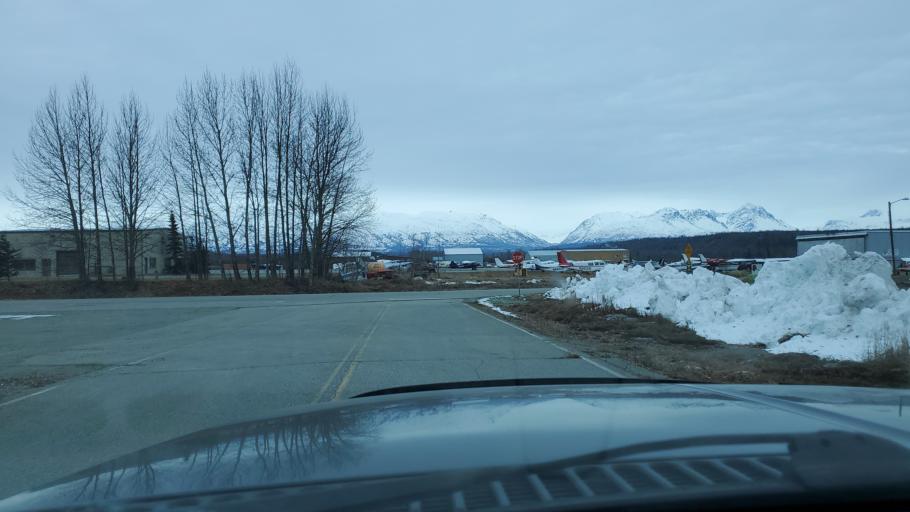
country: US
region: Alaska
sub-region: Matanuska-Susitna Borough
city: Palmer
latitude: 61.5990
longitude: -149.0938
